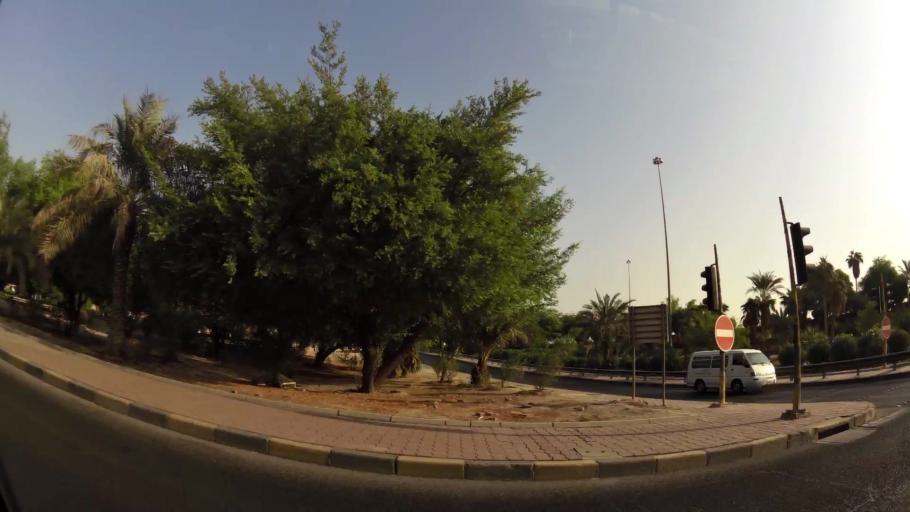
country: KW
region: Muhafazat Hawalli
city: Hawalli
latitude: 29.3442
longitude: 48.0311
